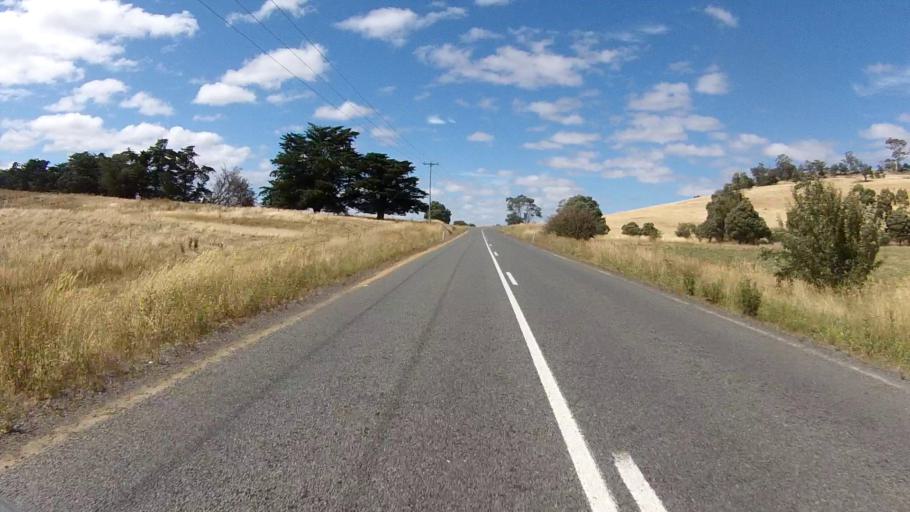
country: AU
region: Tasmania
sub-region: Brighton
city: Old Beach
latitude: -42.5969
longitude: 147.4145
